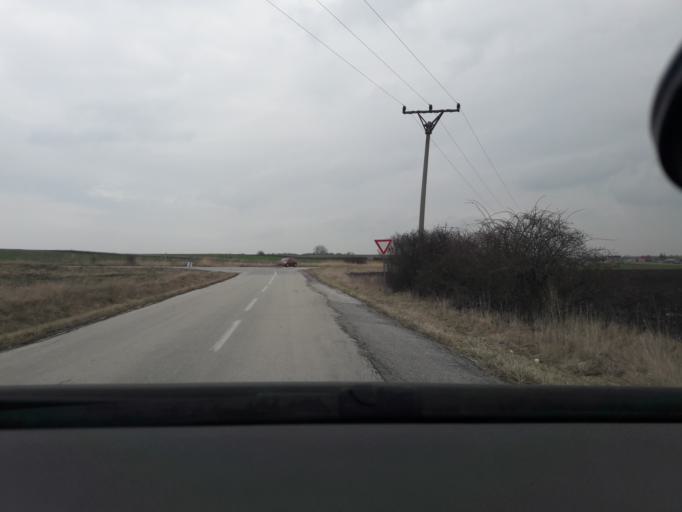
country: SK
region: Bratislavsky
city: Modra
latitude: 48.3971
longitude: 17.3867
